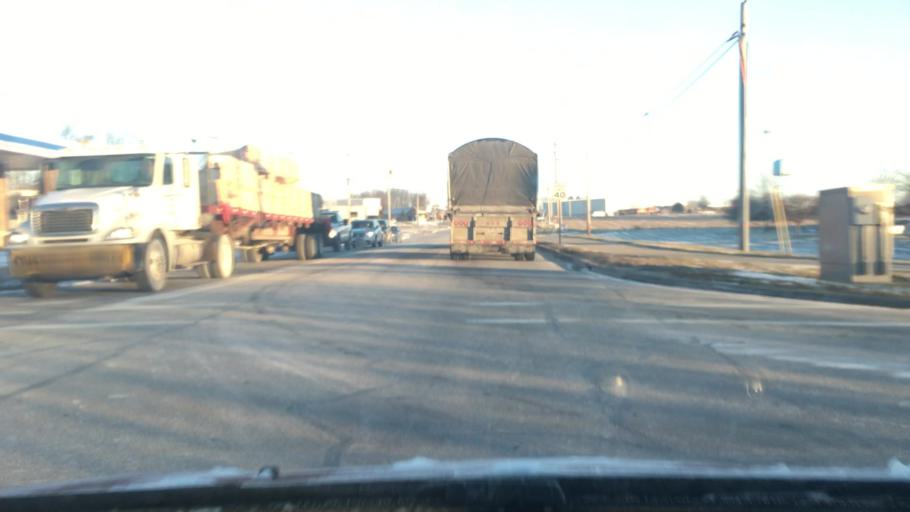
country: US
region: Ohio
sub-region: Wayne County
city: Wooster
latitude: 40.8285
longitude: -81.9085
